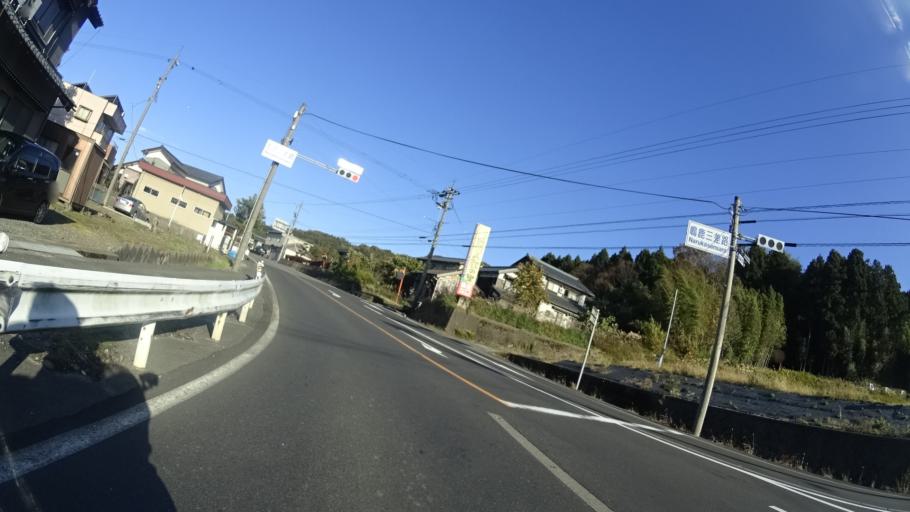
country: JP
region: Fukui
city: Maruoka
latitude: 36.1048
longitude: 136.3282
